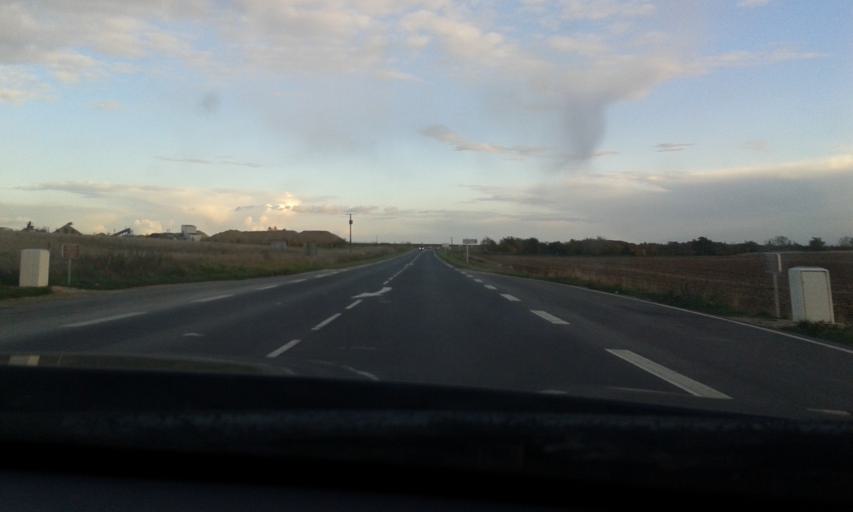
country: FR
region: Centre
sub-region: Departement d'Eure-et-Loir
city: Voves
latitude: 48.2870
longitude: 1.7206
